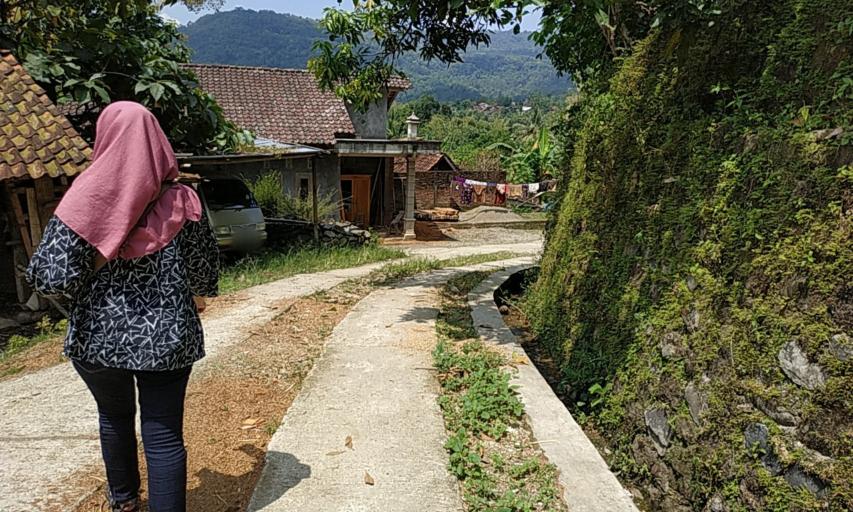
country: ID
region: Central Java
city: Kutoarjo
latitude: -7.6216
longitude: 109.7259
